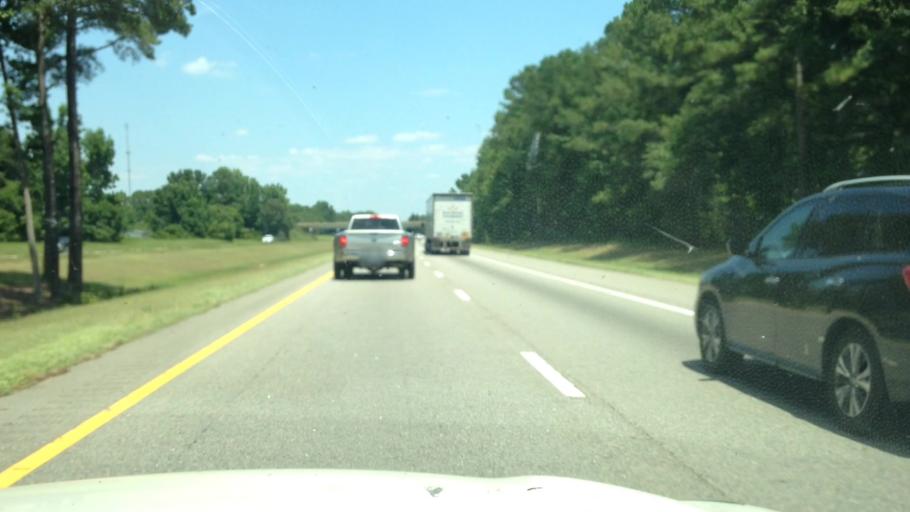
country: US
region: North Carolina
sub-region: Robeson County
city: Rowland
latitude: 34.5336
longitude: -79.2545
